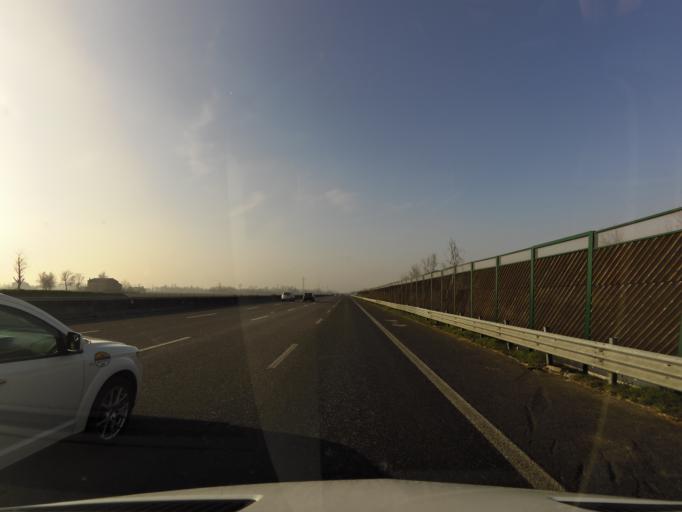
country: IT
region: Emilia-Romagna
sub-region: Provincia di Modena
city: San Damaso
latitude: 44.5922
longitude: 10.9466
